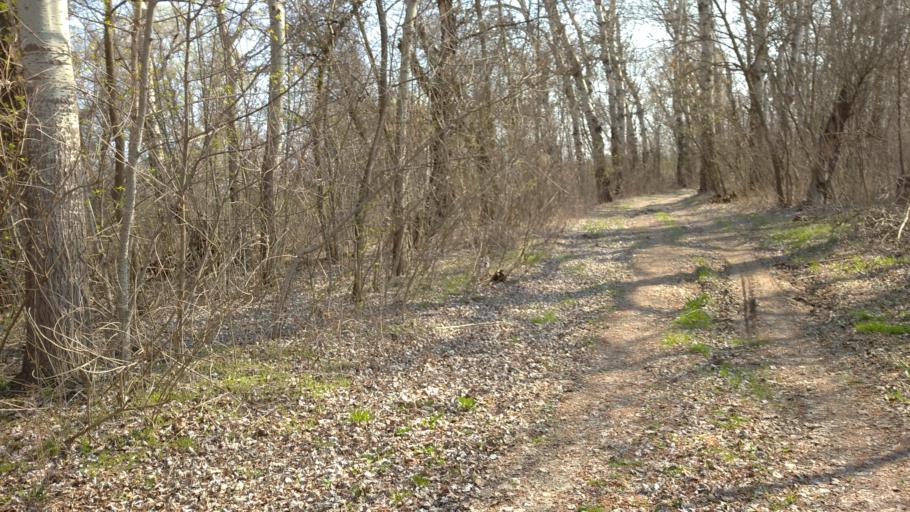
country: HU
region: Csongrad
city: Mindszent
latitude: 46.4865
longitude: 20.2151
